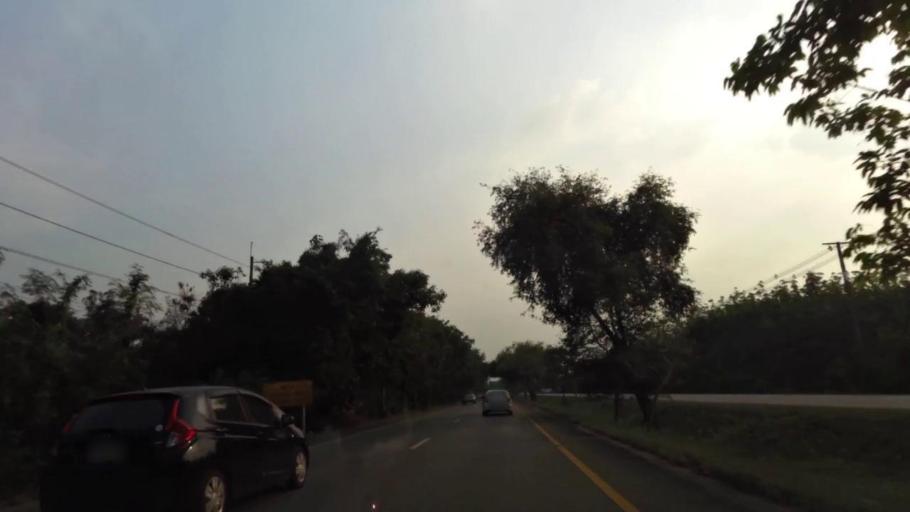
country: TH
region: Chanthaburi
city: Chanthaburi
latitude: 12.5351
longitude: 102.1575
